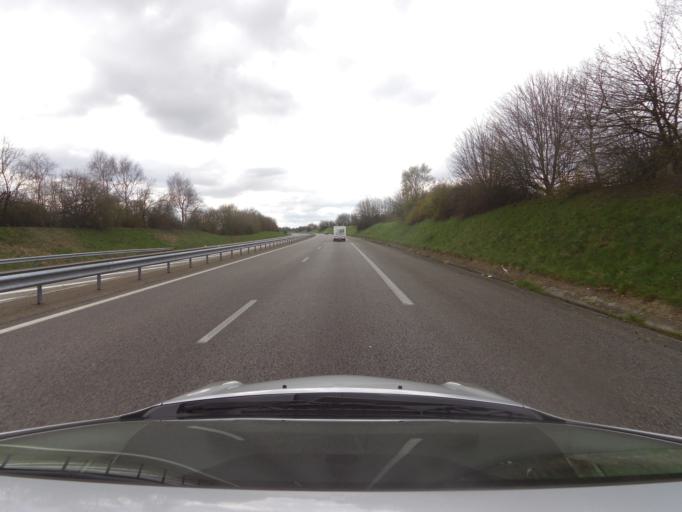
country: FR
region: Haute-Normandie
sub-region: Departement de la Seine-Maritime
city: Saint-Aubin-Routot
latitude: 49.5337
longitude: 0.3153
